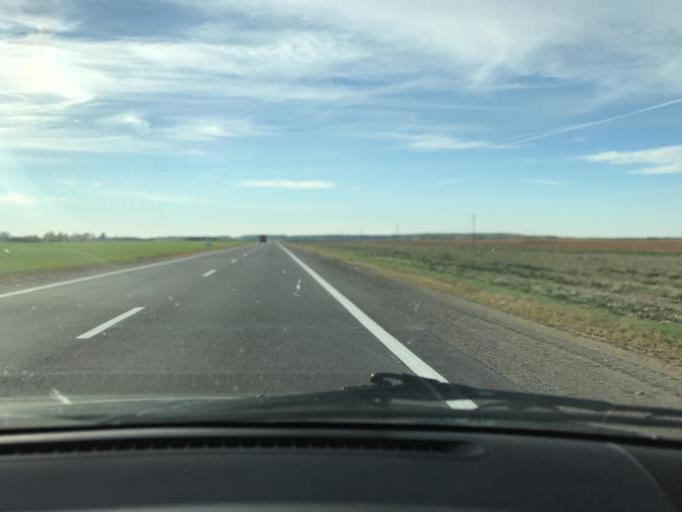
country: BY
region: Brest
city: Ivanava
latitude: 52.1560
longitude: 25.6592
